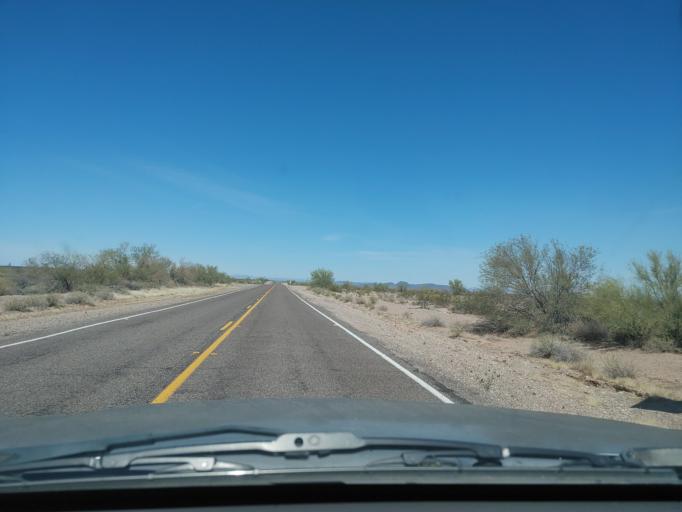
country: US
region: Arizona
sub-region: Maricopa County
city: Gila Bend
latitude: 32.8898
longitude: -113.2400
